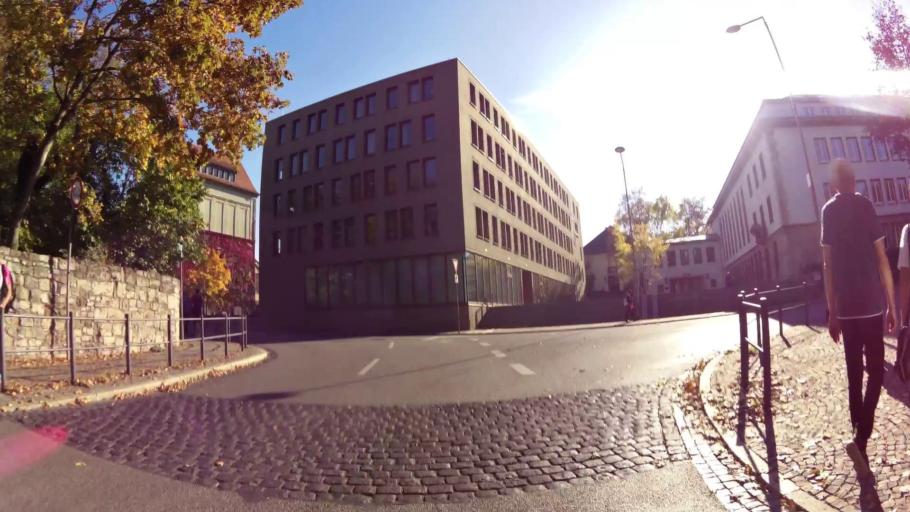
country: DE
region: Thuringia
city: Weimar
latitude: 50.9832
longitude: 11.3212
